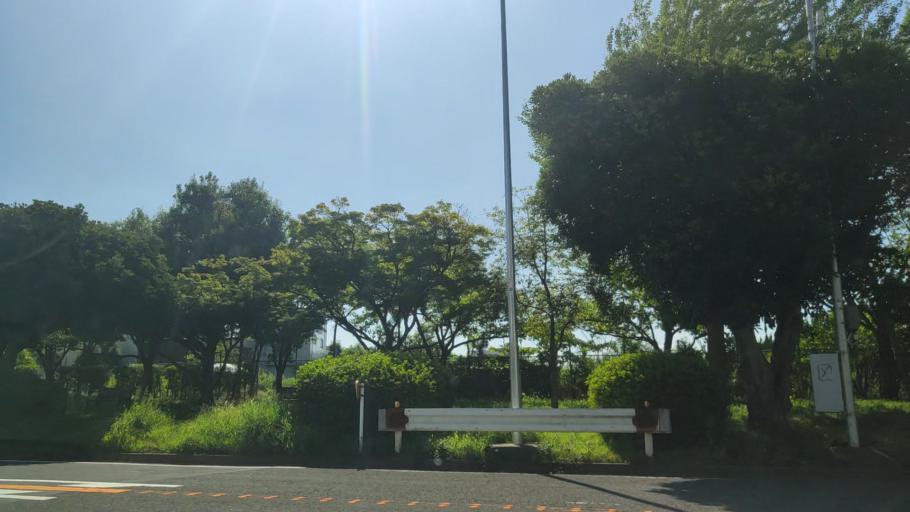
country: JP
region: Kanagawa
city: Yokohama
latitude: 35.5185
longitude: 139.6209
